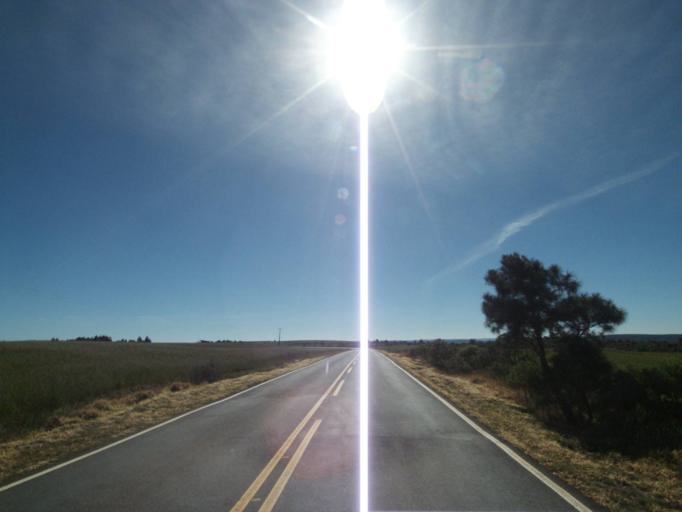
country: BR
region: Parana
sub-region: Castro
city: Castro
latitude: -24.7043
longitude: -50.1936
